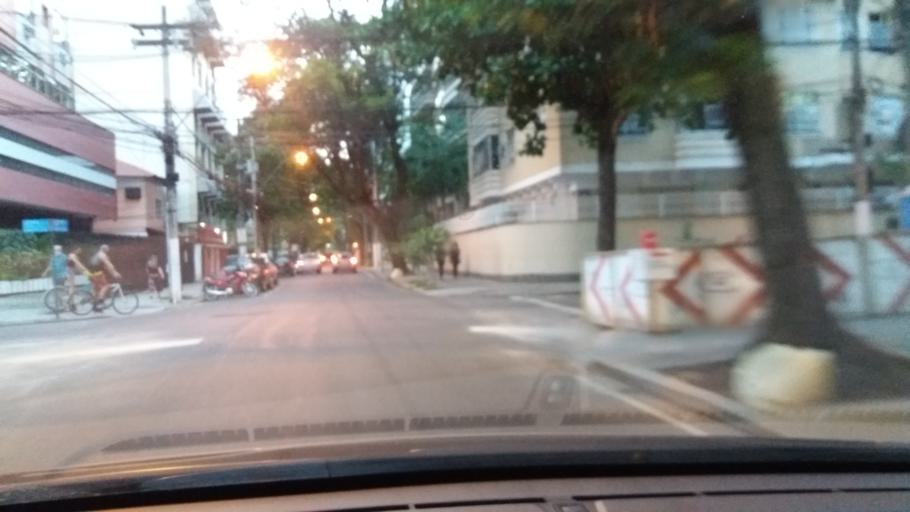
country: BR
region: Rio de Janeiro
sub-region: Niteroi
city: Niteroi
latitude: -22.9026
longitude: -43.1039
